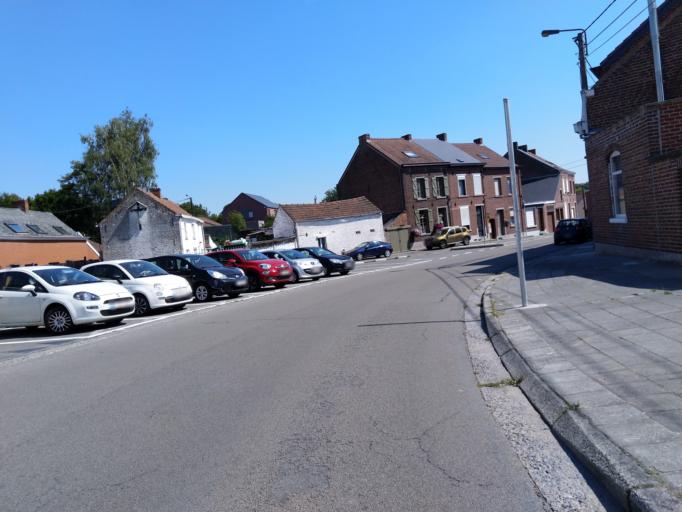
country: BE
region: Wallonia
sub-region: Province du Hainaut
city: Roeulx
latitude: 50.4759
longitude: 4.0987
